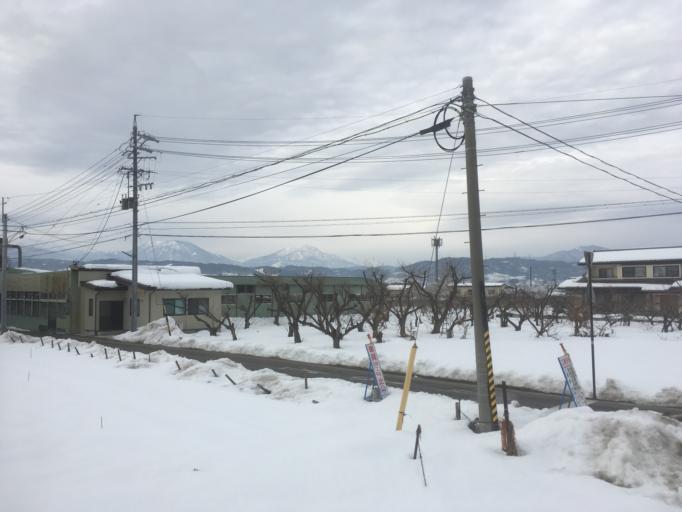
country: JP
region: Nagano
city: Suzaka
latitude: 36.7000
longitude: 138.3145
